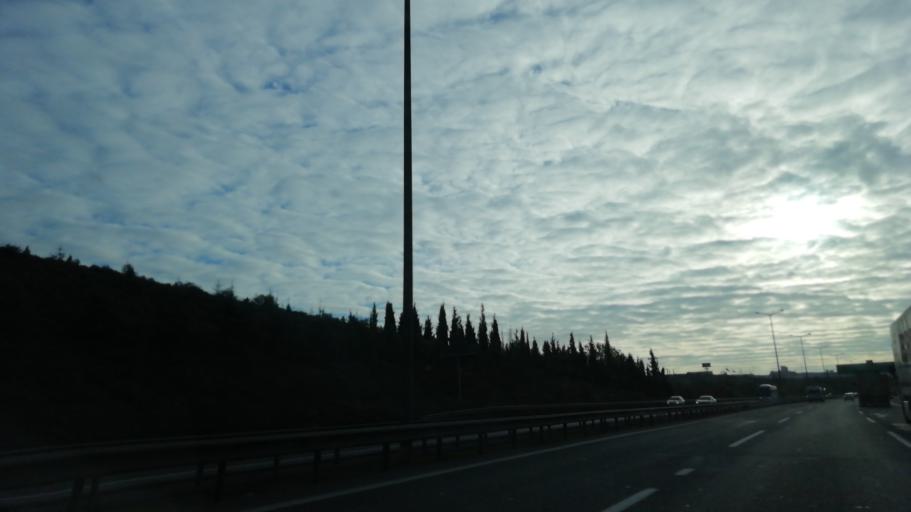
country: TR
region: Kocaeli
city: Balcik
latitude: 40.8743
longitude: 29.3913
